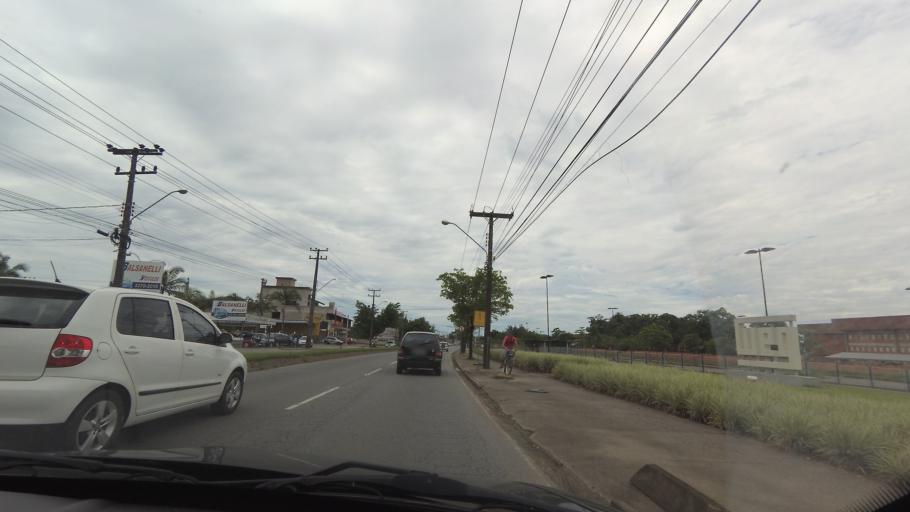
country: BR
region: Santa Catarina
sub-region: Jaragua Do Sul
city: Jaragua do Sul
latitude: -26.4775
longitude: -49.0456
